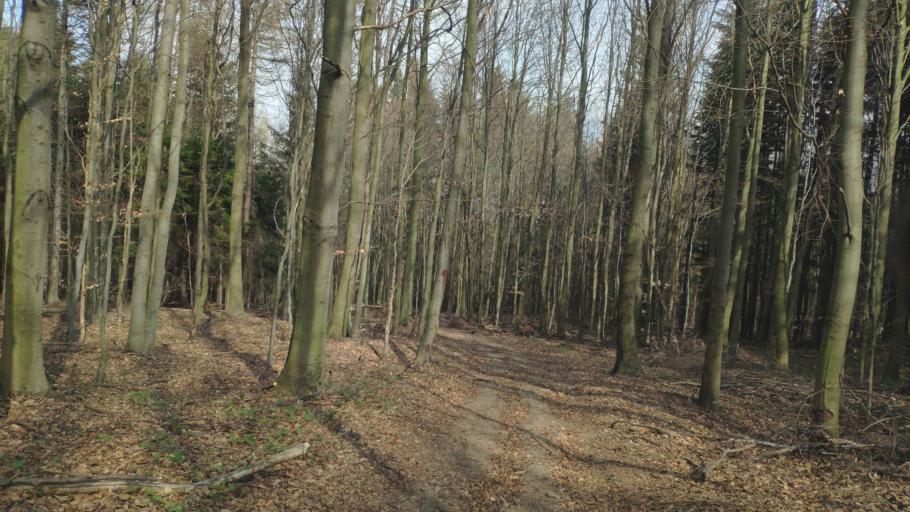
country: SK
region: Kosicky
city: Moldava nad Bodvou
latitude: 48.7376
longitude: 21.0515
